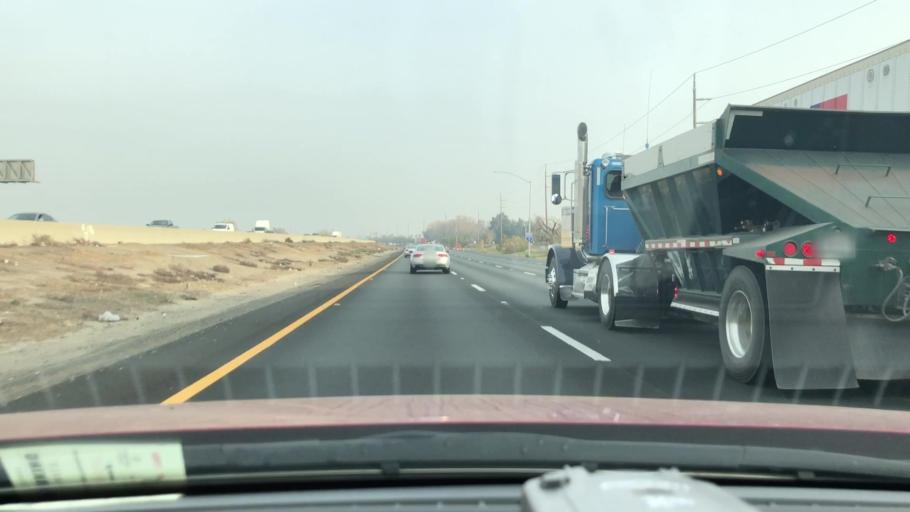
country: US
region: California
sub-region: San Joaquin County
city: Lathrop
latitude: 37.8301
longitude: -121.2885
